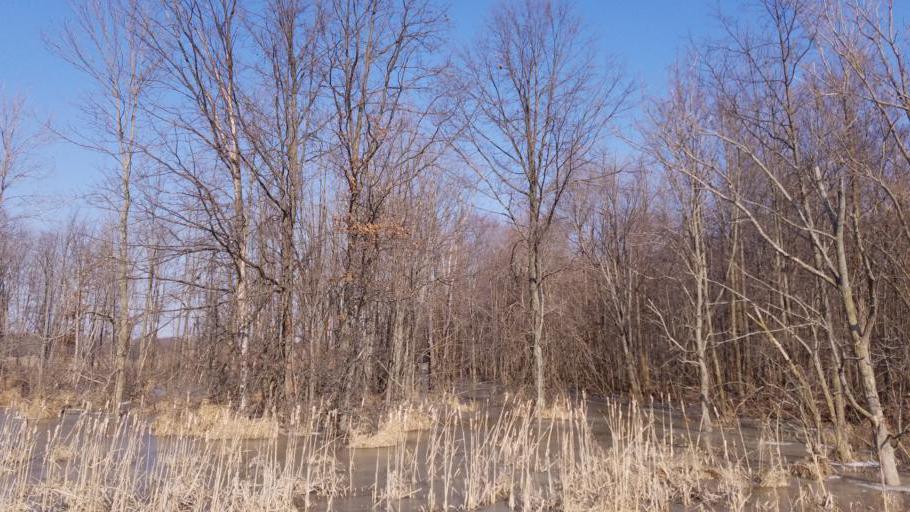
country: US
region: Ohio
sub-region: Richland County
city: Mansfield
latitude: 40.8288
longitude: -82.5427
